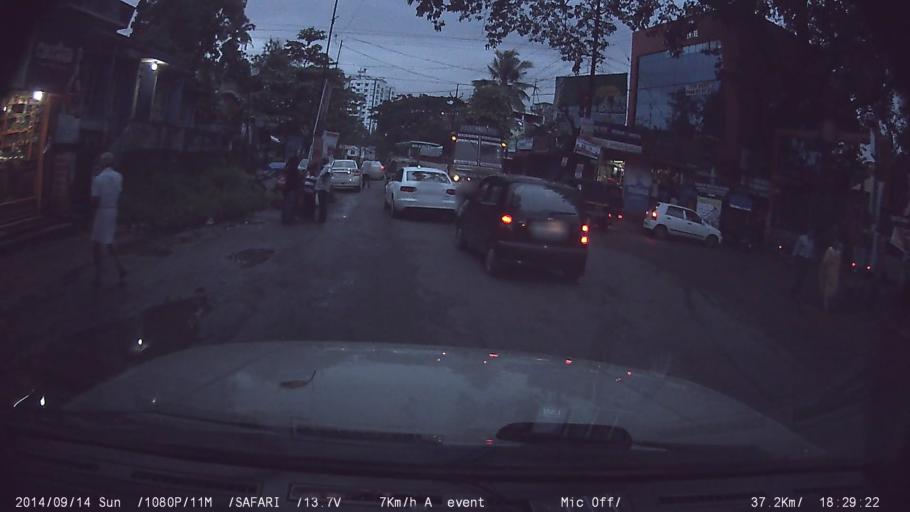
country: IN
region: Kerala
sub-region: Kottayam
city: Kottayam
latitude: 9.6112
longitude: 76.5334
